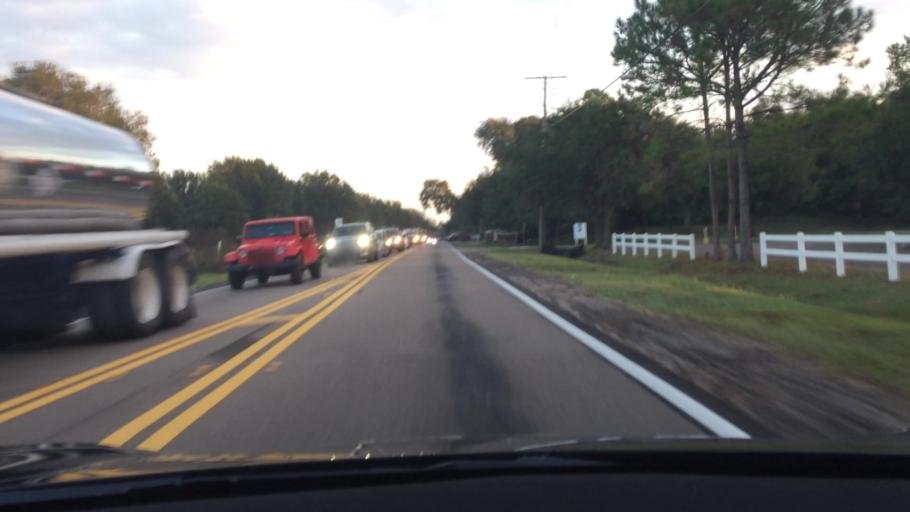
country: US
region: Florida
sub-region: Hillsborough County
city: Citrus Park
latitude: 28.1154
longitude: -82.5801
